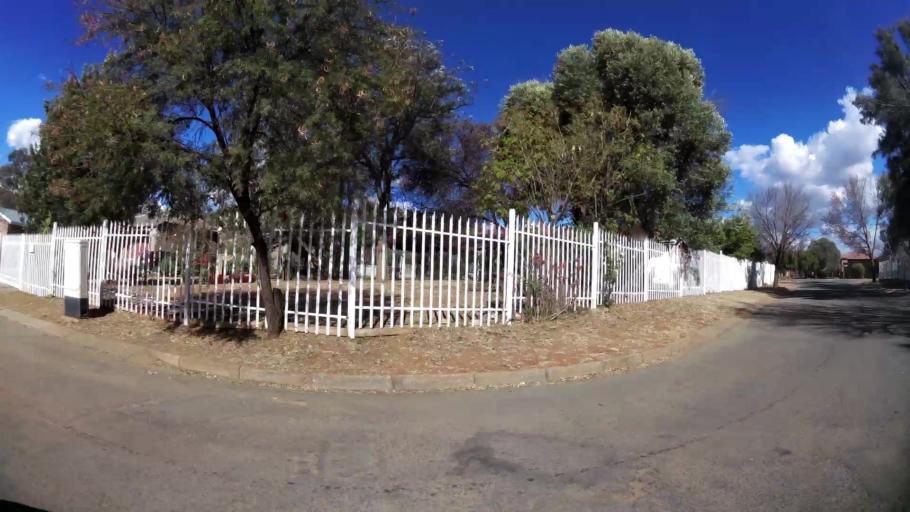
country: ZA
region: North-West
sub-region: Dr Kenneth Kaunda District Municipality
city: Klerksdorp
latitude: -26.8569
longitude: 26.6493
